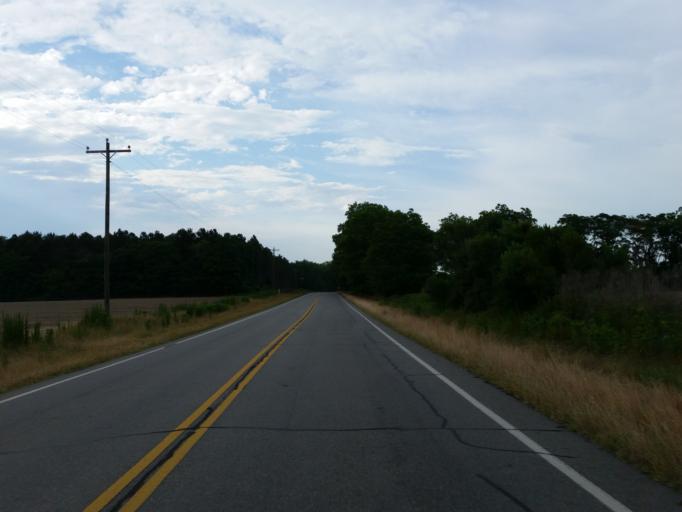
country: US
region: Georgia
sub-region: Dooly County
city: Vienna
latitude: 32.1400
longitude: -83.7975
